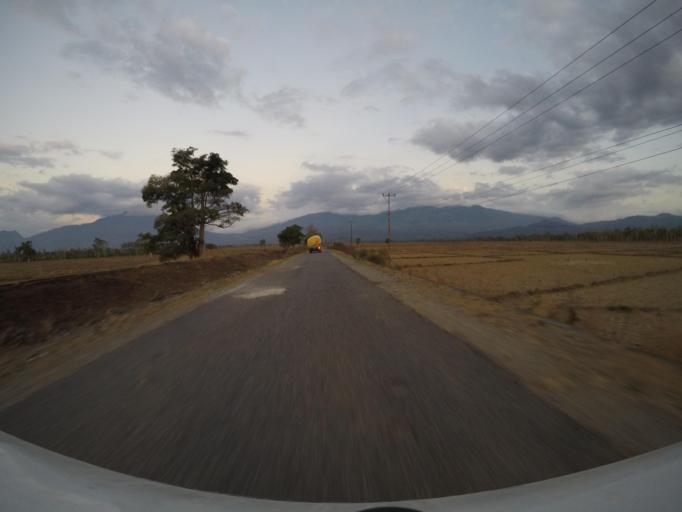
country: TL
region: Bobonaro
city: Maliana
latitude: -8.9797
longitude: 125.1492
